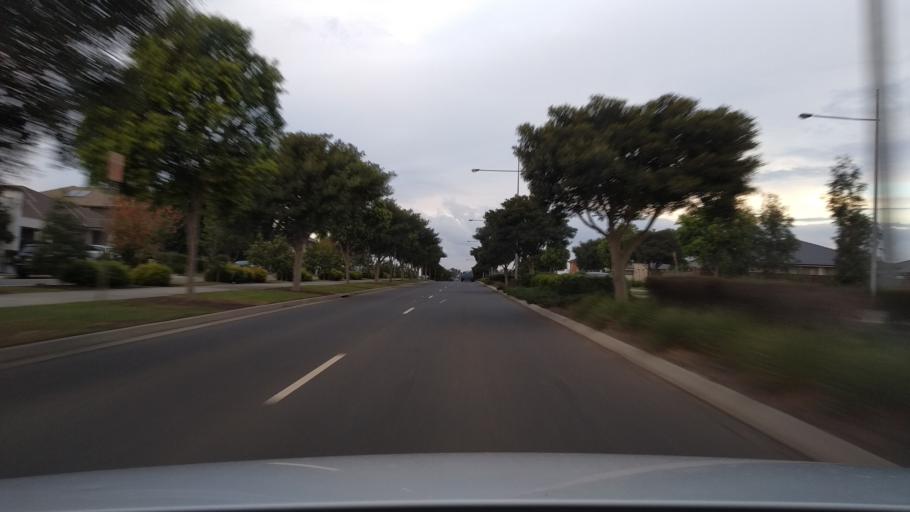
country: AU
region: New South Wales
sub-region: Camden
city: Narellan
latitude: -34.0027
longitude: 150.7395
